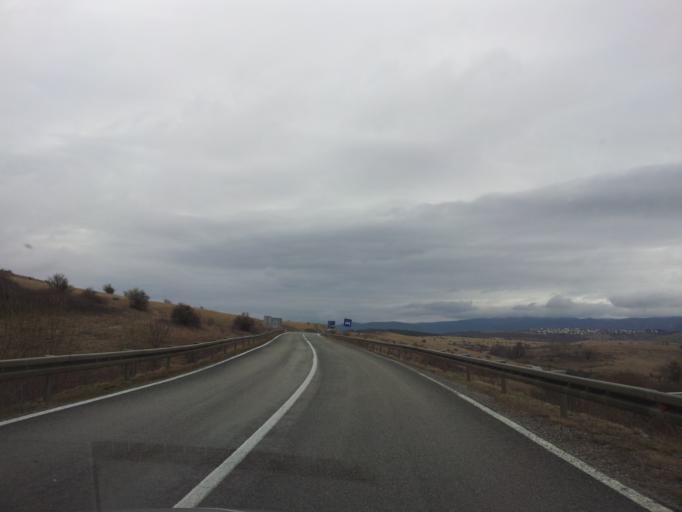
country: HR
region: Zadarska
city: Gracac
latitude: 44.4968
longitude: 15.7466
